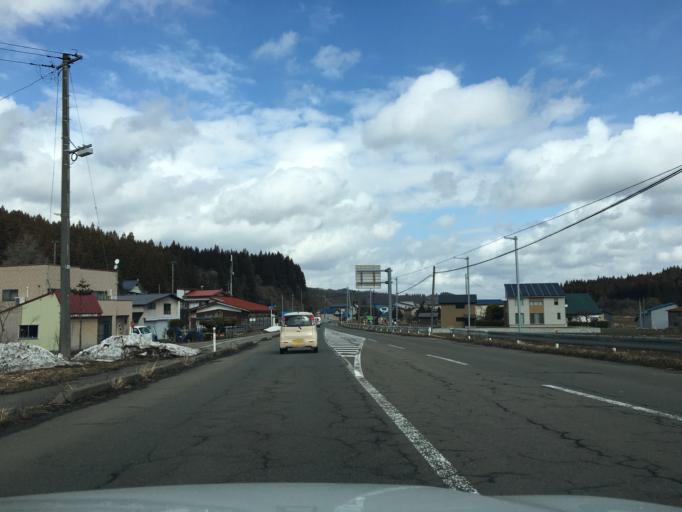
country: JP
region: Akita
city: Takanosu
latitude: 40.0322
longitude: 140.2747
